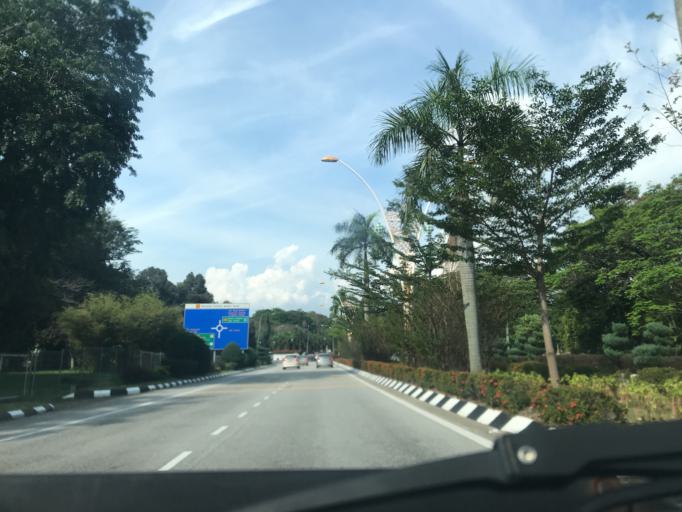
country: MY
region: Perak
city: Ipoh
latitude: 4.5970
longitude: 101.1037
